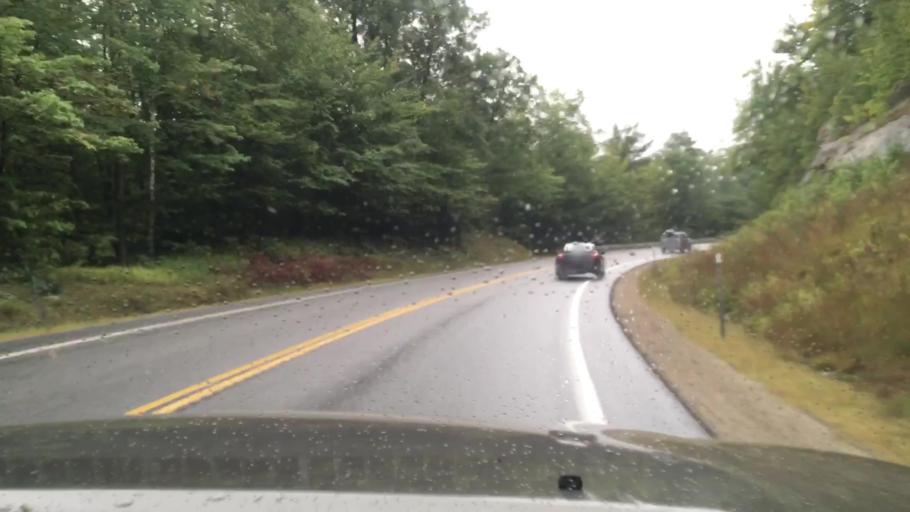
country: US
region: New Hampshire
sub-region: Cheshire County
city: Harrisville
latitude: 43.0645
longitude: -72.0676
